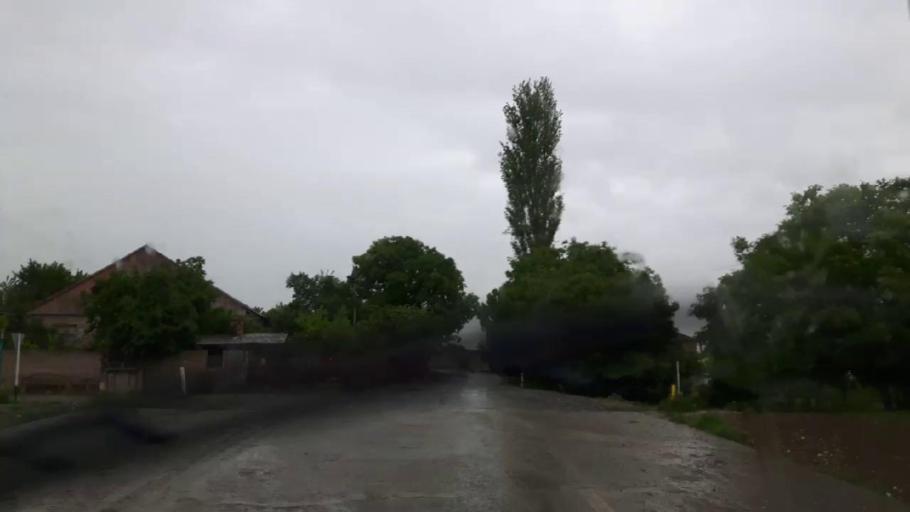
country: GE
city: Agara
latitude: 41.9828
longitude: 43.9571
